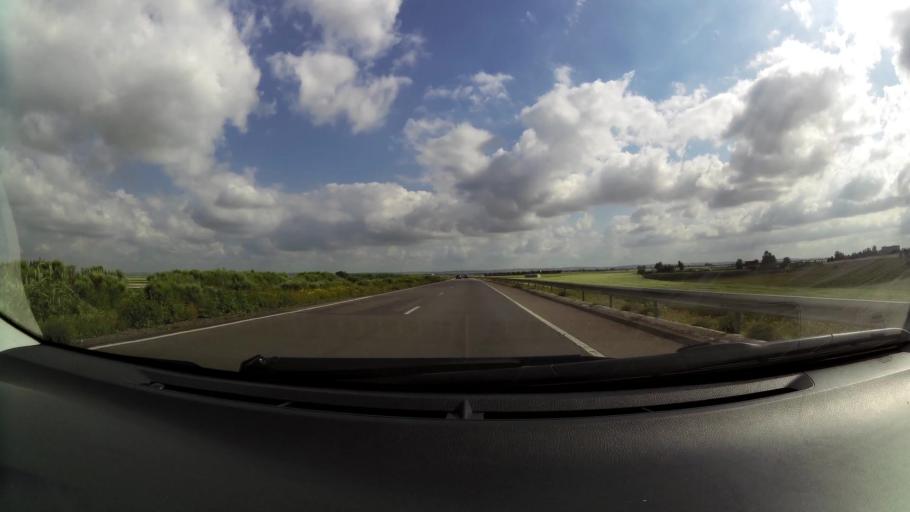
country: MA
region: Chaouia-Ouardigha
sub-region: Settat Province
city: Berrechid
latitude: 33.1956
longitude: -7.5761
